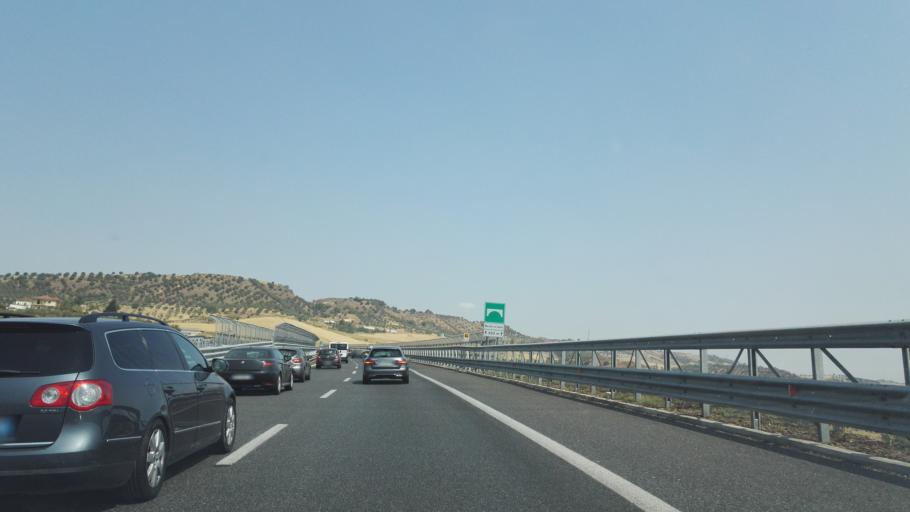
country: IT
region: Calabria
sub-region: Provincia di Cosenza
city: Tarsia
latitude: 39.5919
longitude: 16.2459
